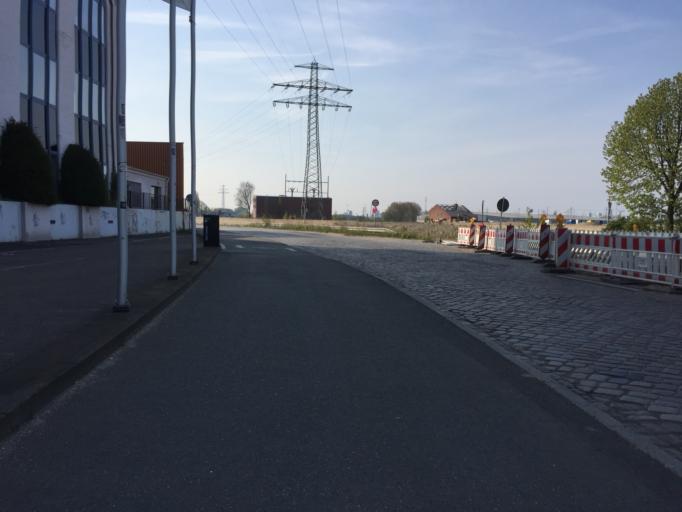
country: DE
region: Hamburg
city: Kleiner Grasbrook
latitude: 53.5301
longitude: 9.9697
